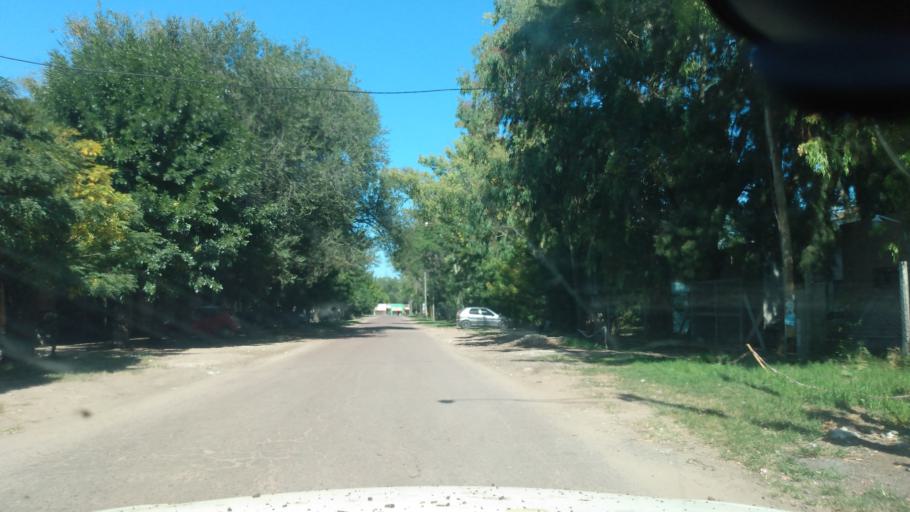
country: AR
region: Buenos Aires
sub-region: Partido de Lujan
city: Lujan
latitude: -34.4886
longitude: -59.0765
